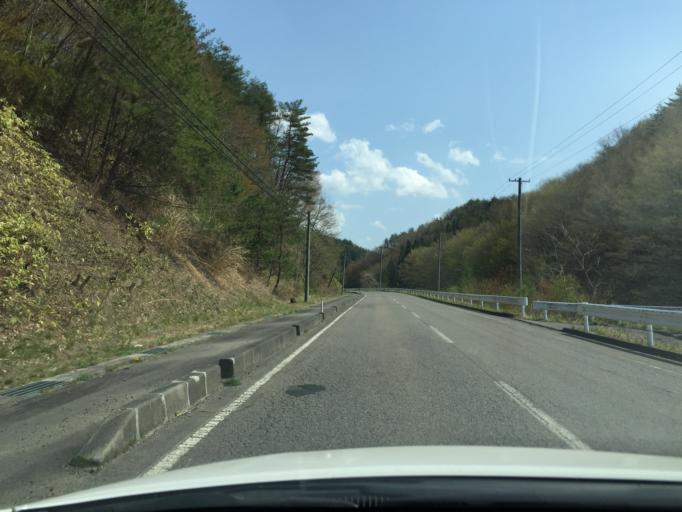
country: JP
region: Fukushima
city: Namie
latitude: 37.4151
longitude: 140.7943
